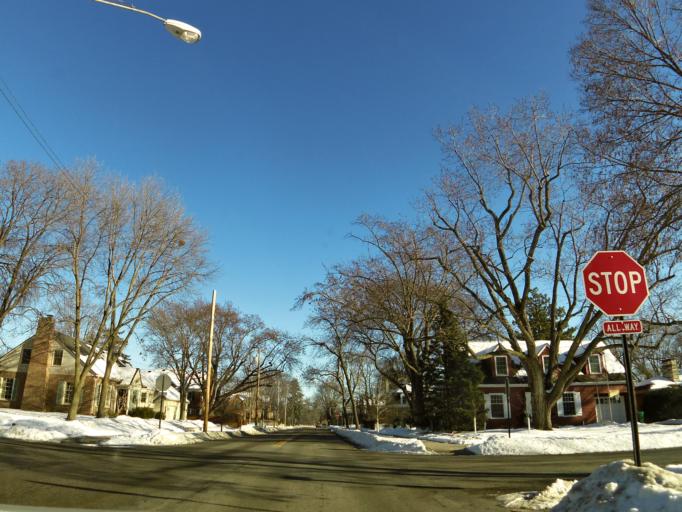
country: US
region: Minnesota
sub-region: Hennepin County
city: Saint Louis Park
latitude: 44.9342
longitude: -93.3318
